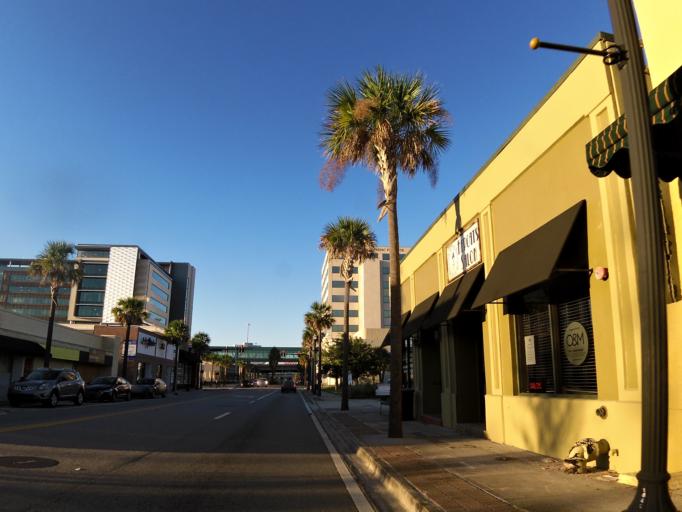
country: US
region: Florida
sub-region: Duval County
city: Jacksonville
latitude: 30.3113
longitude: -81.6605
